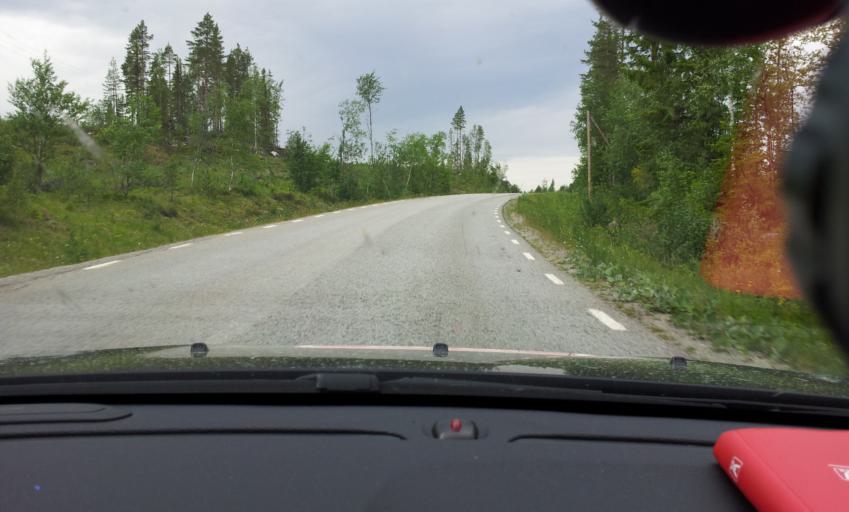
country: SE
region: Jaemtland
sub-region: Bergs Kommun
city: Hoverberg
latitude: 62.6695
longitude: 14.7226
